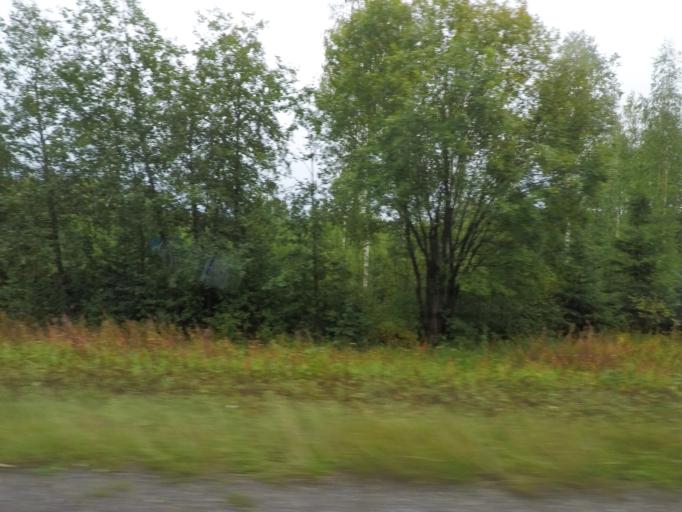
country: FI
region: Southern Savonia
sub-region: Pieksaemaeki
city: Joroinen
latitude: 62.1216
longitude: 27.8392
